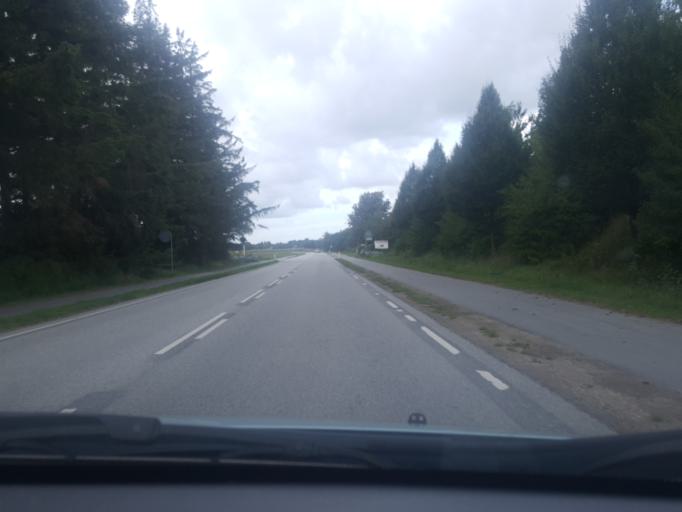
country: DK
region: Zealand
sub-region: Guldborgsund Kommune
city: Nykobing Falster
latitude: 54.6980
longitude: 11.9485
